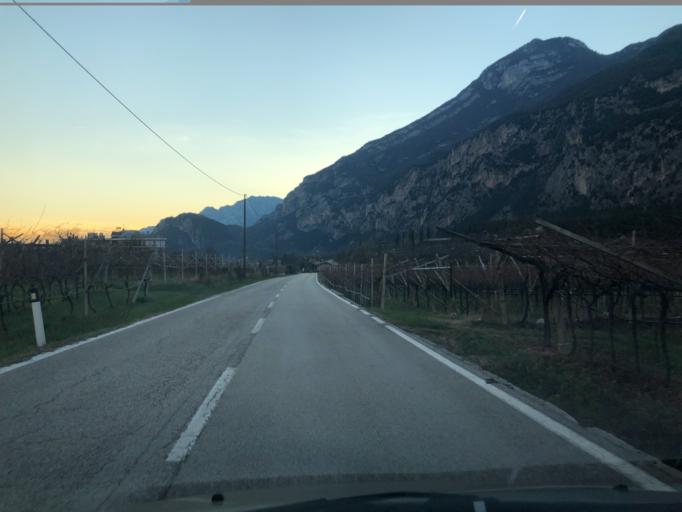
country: IT
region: Trentino-Alto Adige
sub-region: Provincia di Trento
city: Dro
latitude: 45.9716
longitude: 10.9214
